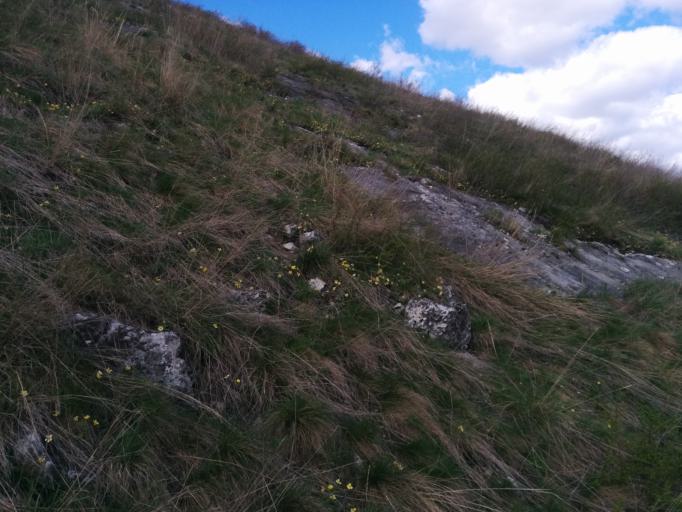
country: RU
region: Bashkortostan
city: Sterlitamak
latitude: 53.7417
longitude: 56.0996
